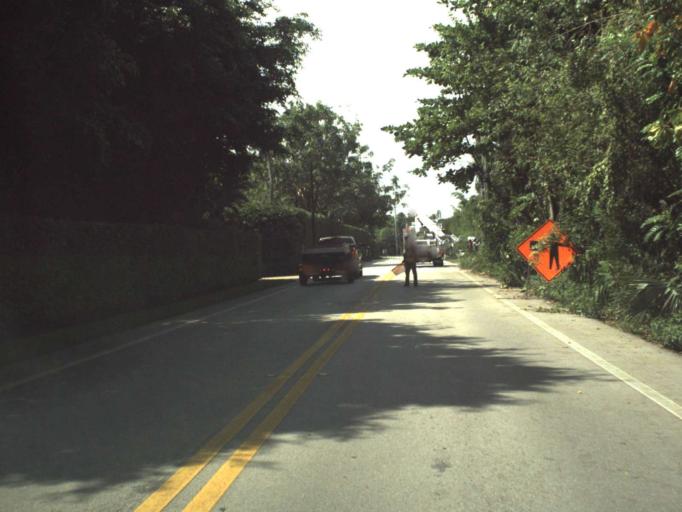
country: US
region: Florida
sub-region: Palm Beach County
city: Palm Beach
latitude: 26.6732
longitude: -80.0382
